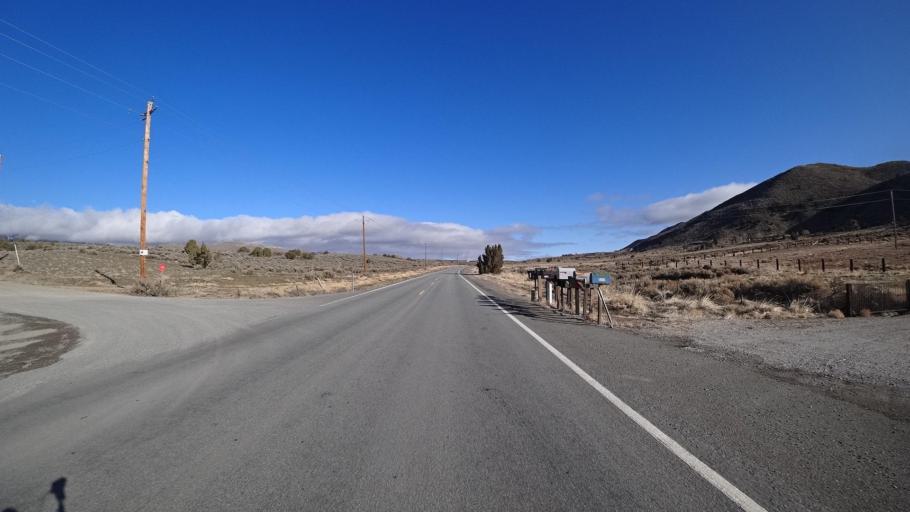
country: US
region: Nevada
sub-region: Washoe County
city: Cold Springs
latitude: 39.7428
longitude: -119.8852
